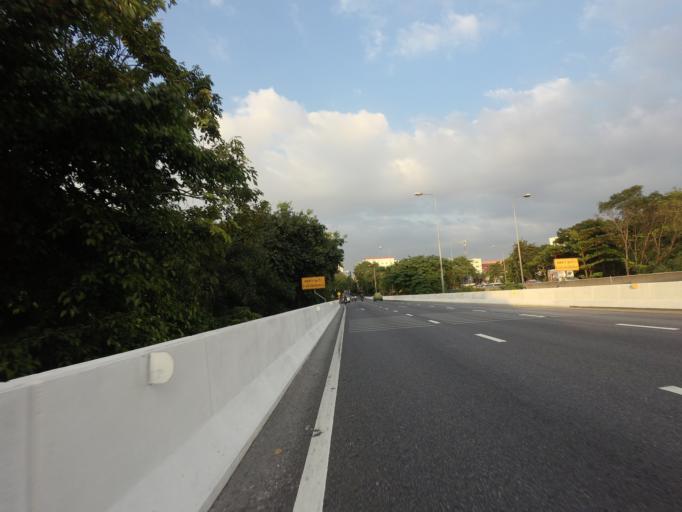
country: TH
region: Bangkok
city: Khlong San
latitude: 13.7401
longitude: 100.4991
